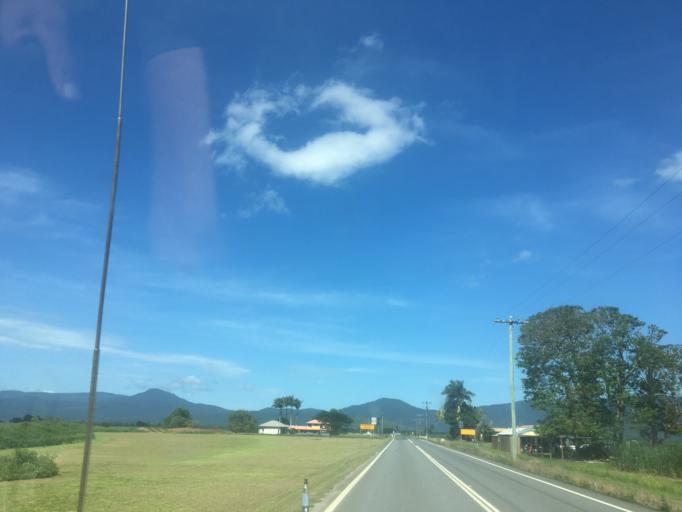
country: AU
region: Queensland
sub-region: Cairns
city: Woree
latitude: -17.0617
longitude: 145.7618
